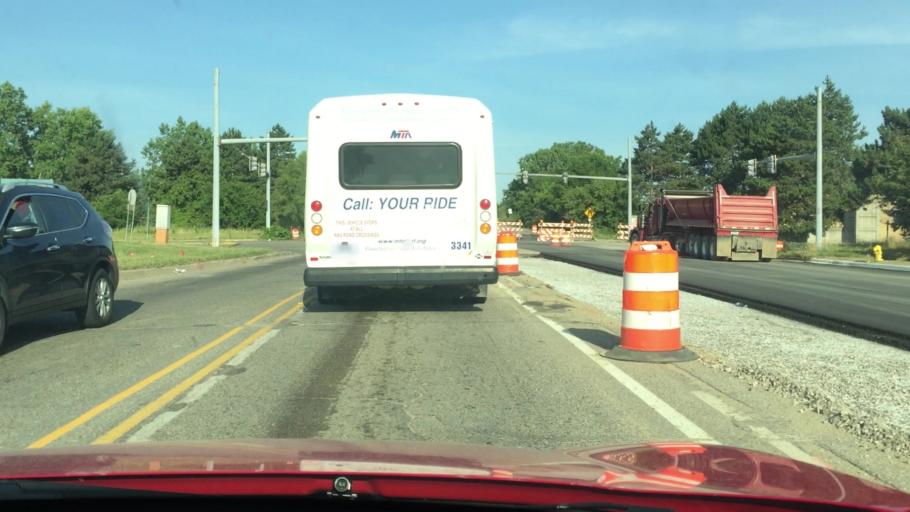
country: US
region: Michigan
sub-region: Genesee County
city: Beecher
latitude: 43.0540
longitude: -83.6758
